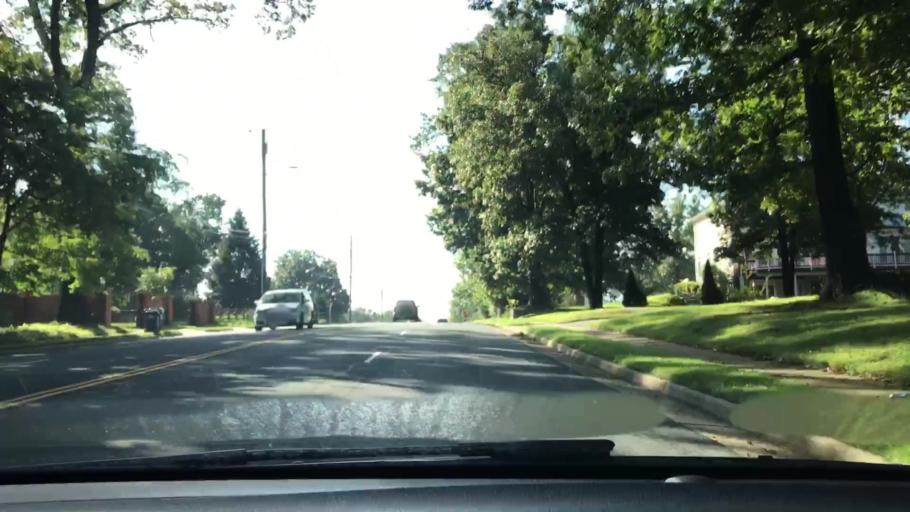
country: US
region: Virginia
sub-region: Fairfax County
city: Annandale
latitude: 38.8403
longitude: -77.1994
